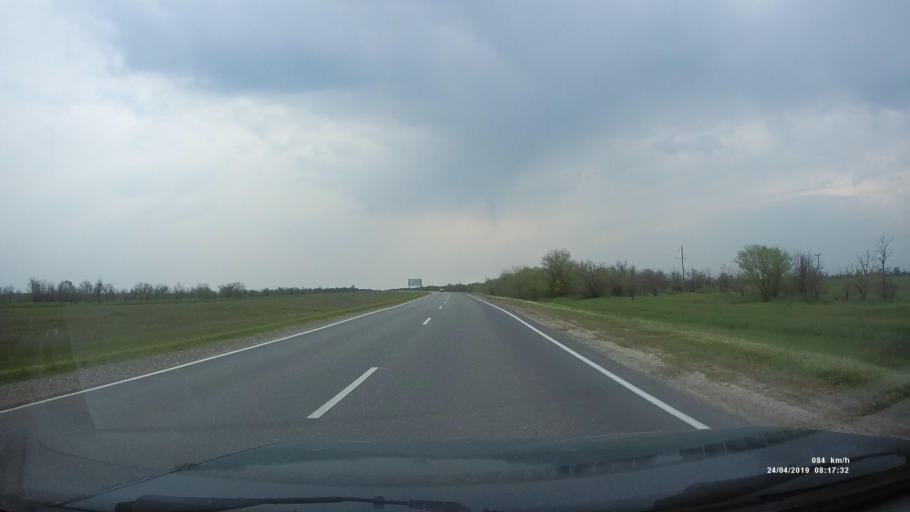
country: RU
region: Kalmykiya
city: Priyutnoye
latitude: 46.0976
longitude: 43.6315
